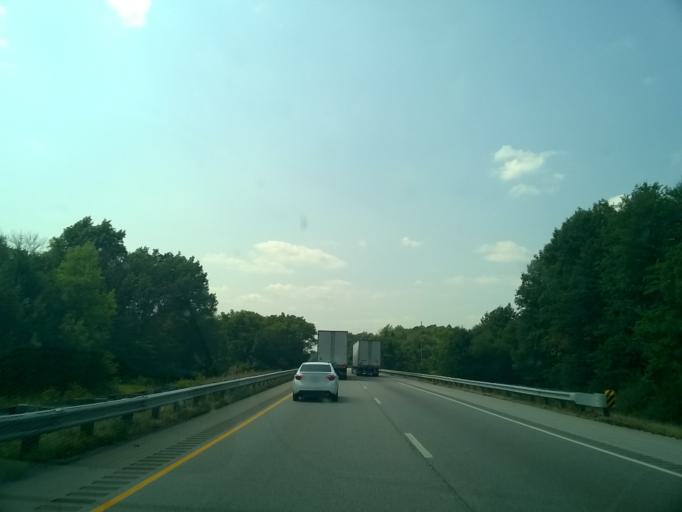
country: US
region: Indiana
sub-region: Vigo County
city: Seelyville
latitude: 39.4455
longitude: -87.2587
